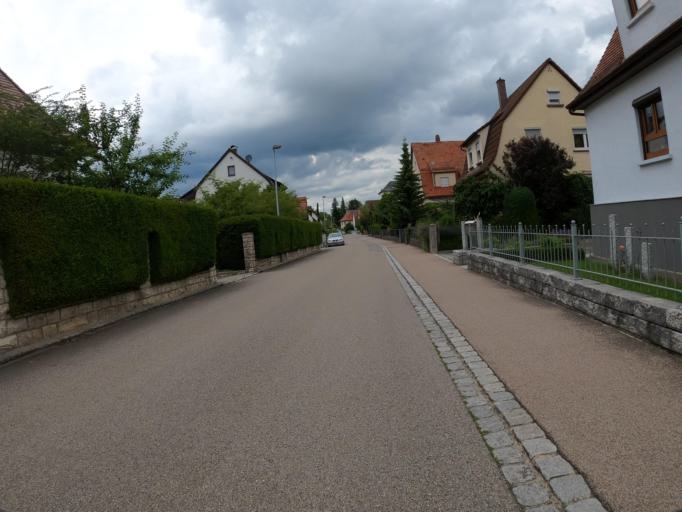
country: DE
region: Baden-Wuerttemberg
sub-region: Tuebingen Region
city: Langenau
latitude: 48.4970
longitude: 10.1272
